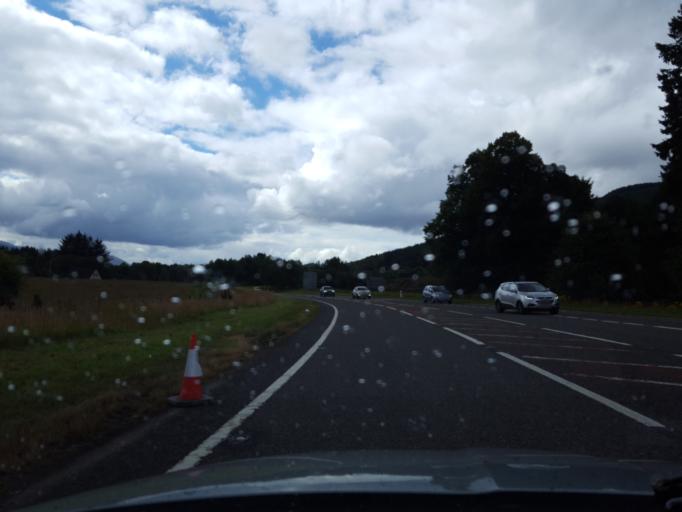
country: GB
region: Scotland
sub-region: Highland
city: Aviemore
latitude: 57.2471
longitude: -3.8028
